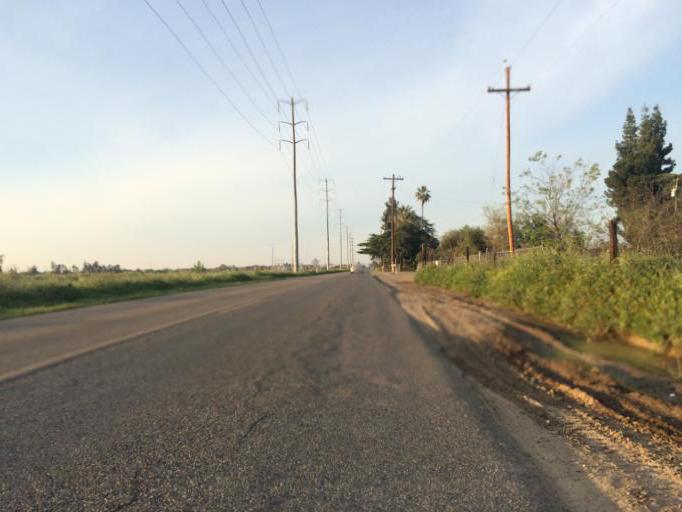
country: US
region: California
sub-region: Fresno County
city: Tarpey Village
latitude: 36.7728
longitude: -119.6732
